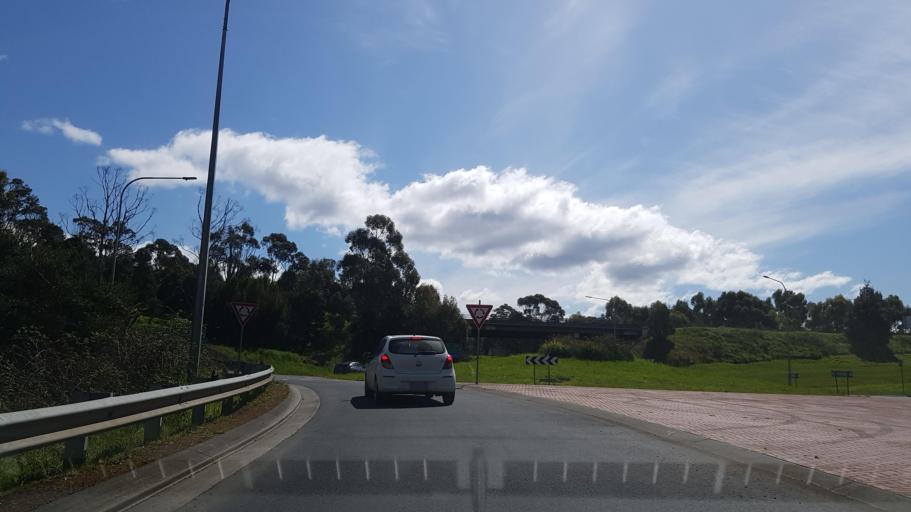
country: AU
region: Tasmania
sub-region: Kingborough
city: Kingston
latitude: -42.9715
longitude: 147.3104
